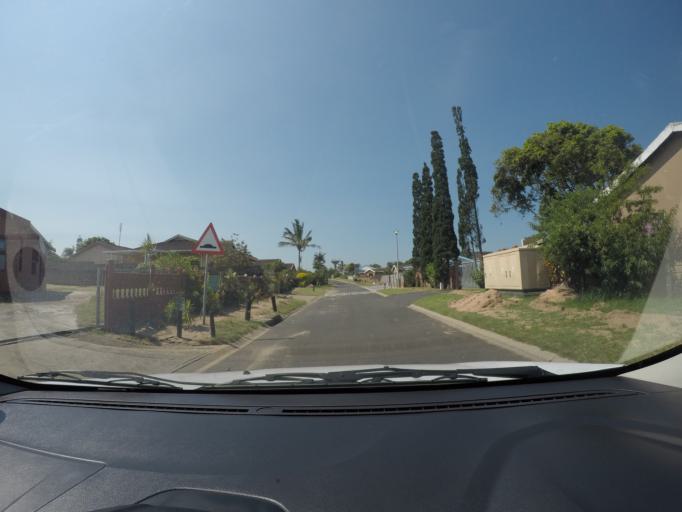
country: ZA
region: KwaZulu-Natal
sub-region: uThungulu District Municipality
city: Richards Bay
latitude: -28.7271
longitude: 32.0407
